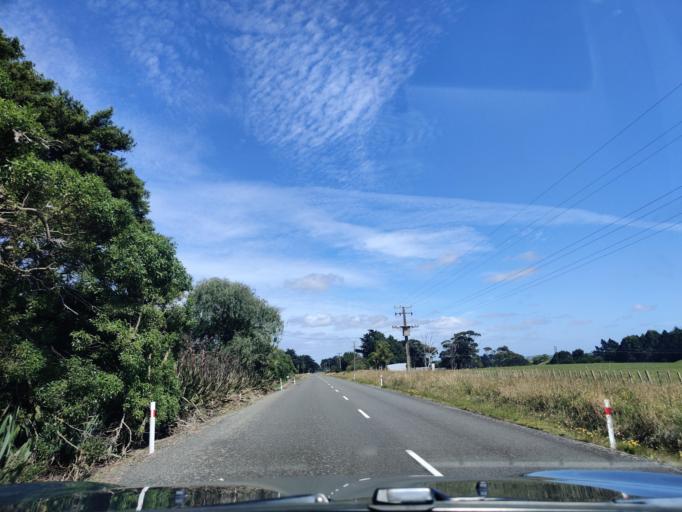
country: NZ
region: Manawatu-Wanganui
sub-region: Rangitikei District
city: Bulls
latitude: -40.1915
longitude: 175.4662
